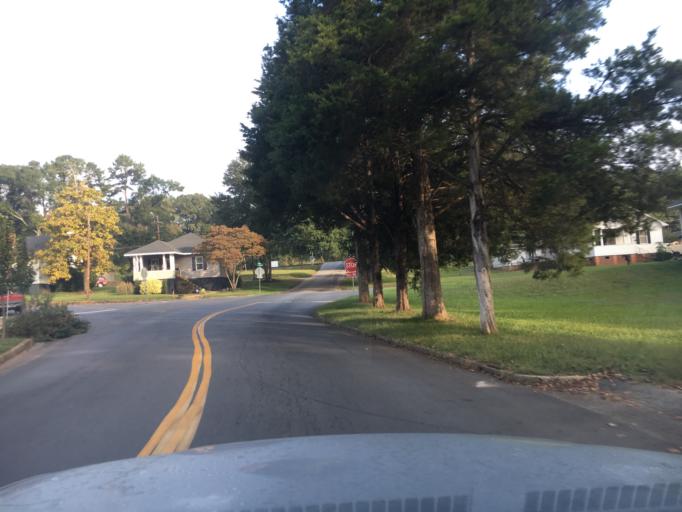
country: US
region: South Carolina
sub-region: Spartanburg County
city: Lyman
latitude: 34.9468
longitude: -82.1305
